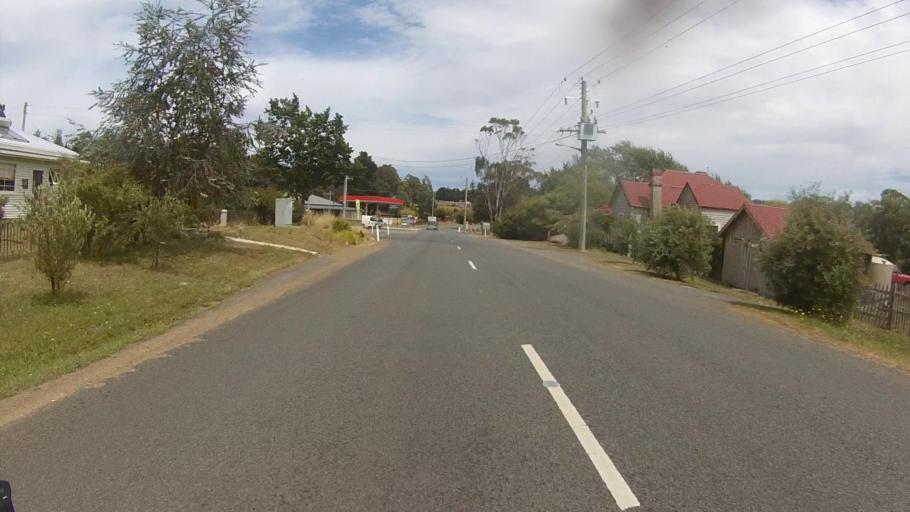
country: AU
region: Tasmania
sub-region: Sorell
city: Sorell
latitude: -42.8195
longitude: 147.8029
